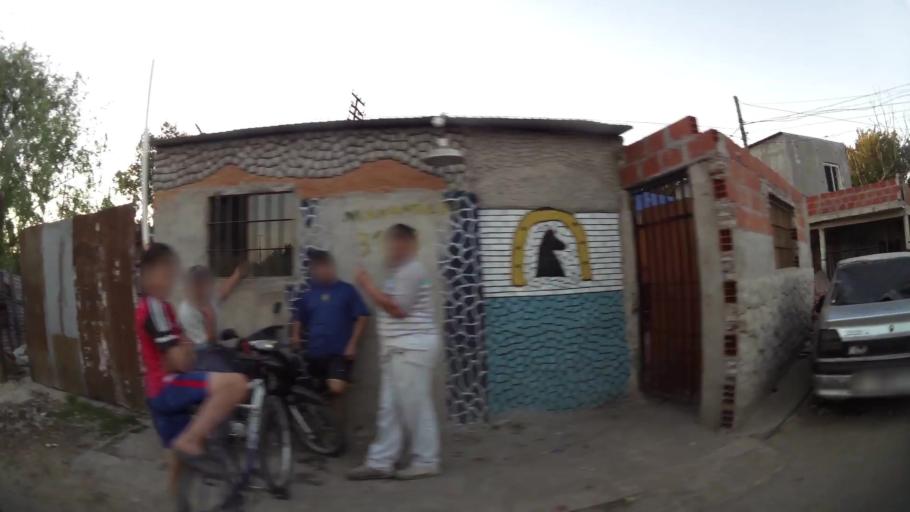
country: AR
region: Santa Fe
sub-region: Departamento de Rosario
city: Rosario
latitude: -32.9651
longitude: -60.6914
